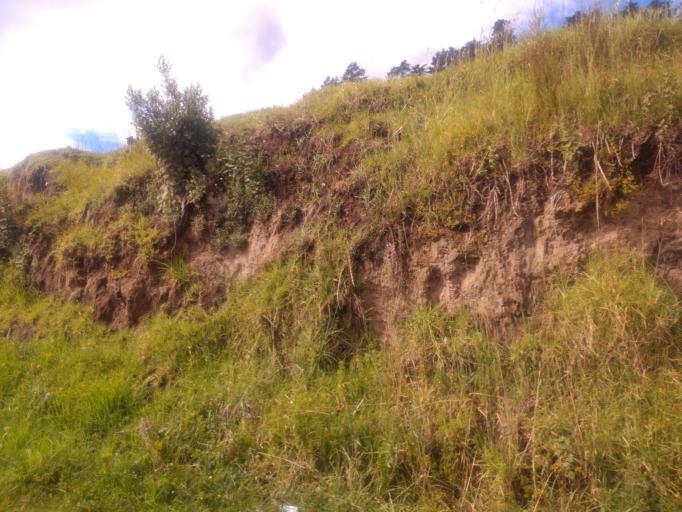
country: GT
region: Quetzaltenango
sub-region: Municipio de La Esperanza
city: La Esperanza
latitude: 14.8568
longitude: -91.5709
